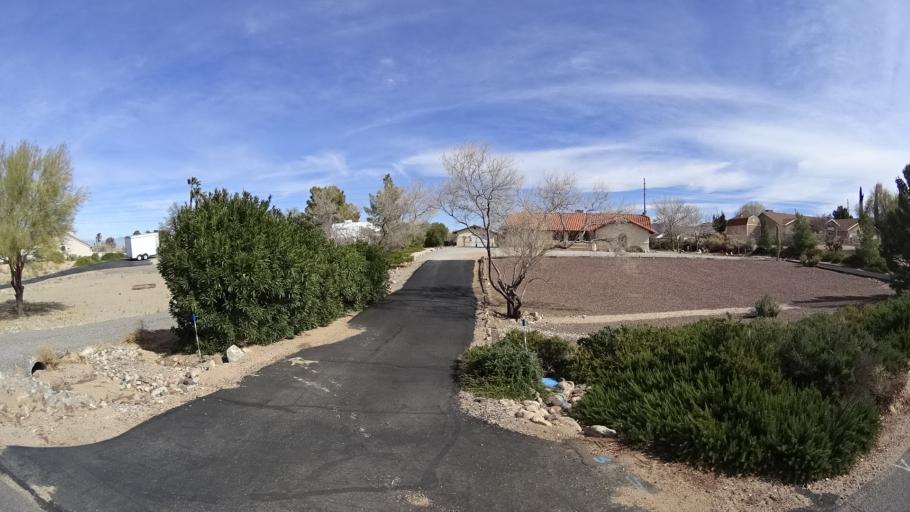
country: US
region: Arizona
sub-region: Mohave County
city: Kingman
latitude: 35.1934
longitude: -113.9878
